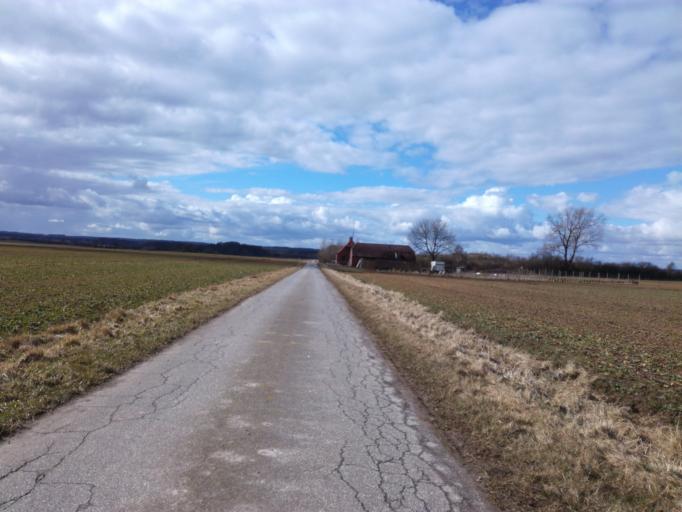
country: DK
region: South Denmark
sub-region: Fredericia Kommune
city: Fredericia
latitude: 55.5992
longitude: 9.7389
